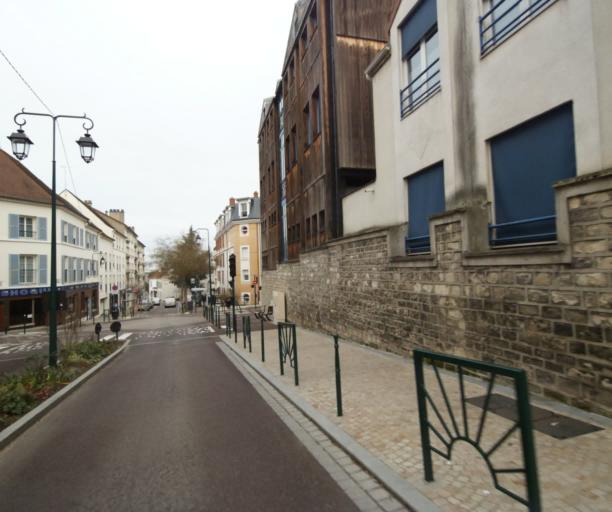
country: FR
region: Ile-de-France
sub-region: Departement des Hauts-de-Seine
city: Rueil-Malmaison
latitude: 48.8765
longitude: 2.1855
